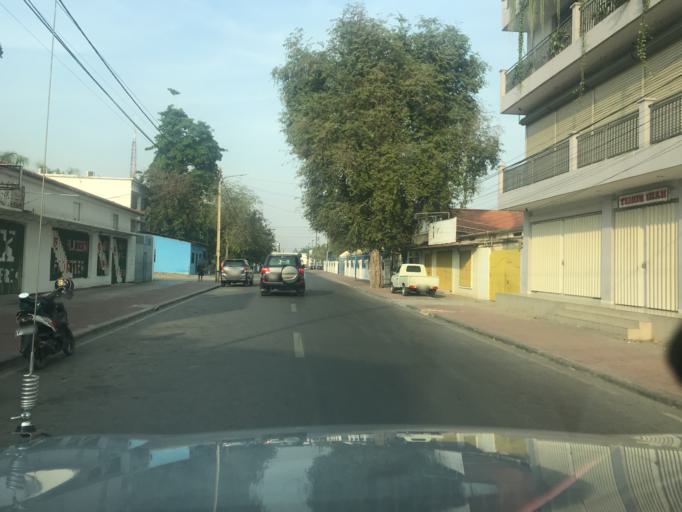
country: TL
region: Dili
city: Dili
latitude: -8.5533
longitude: 125.5807
